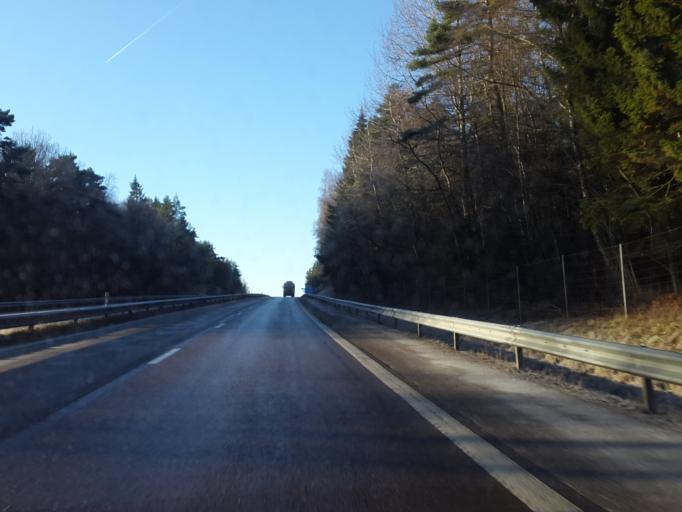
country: SE
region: Vaestra Goetaland
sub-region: Alingsas Kommun
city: Ingared
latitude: 57.8599
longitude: 12.4796
